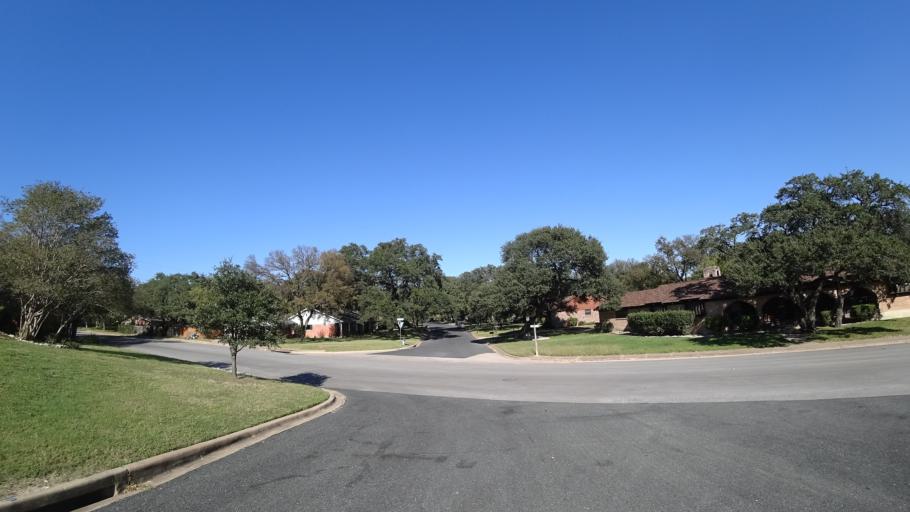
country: US
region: Texas
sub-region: Williamson County
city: Jollyville
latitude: 30.3757
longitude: -97.7424
